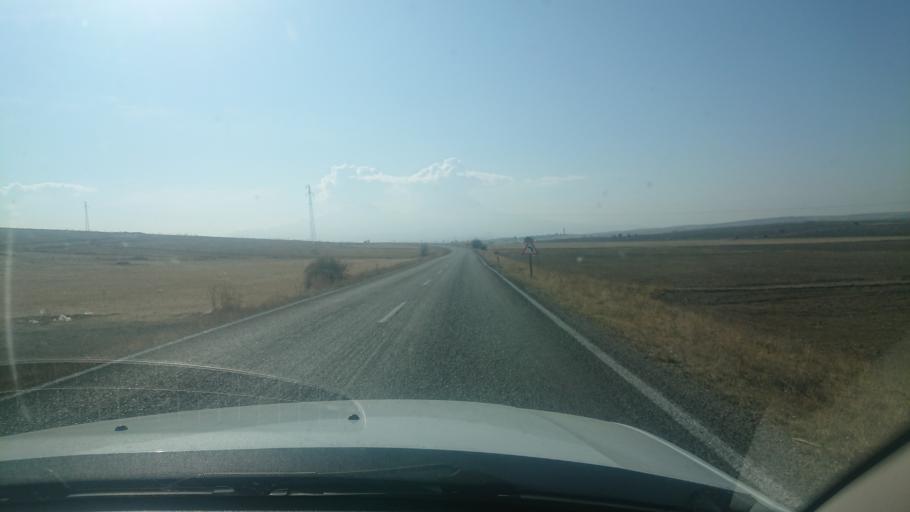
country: TR
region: Aksaray
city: Guzelyurt
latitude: 38.3018
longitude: 34.3198
